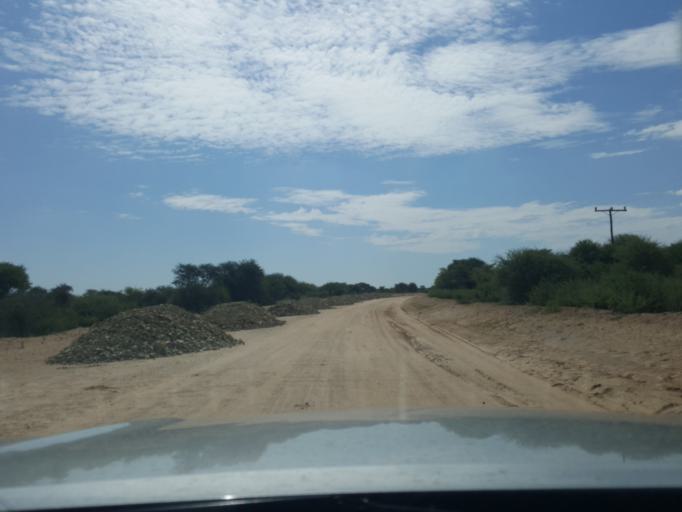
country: BW
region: Kweneng
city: Letlhakeng
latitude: -24.0430
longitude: 25.0125
